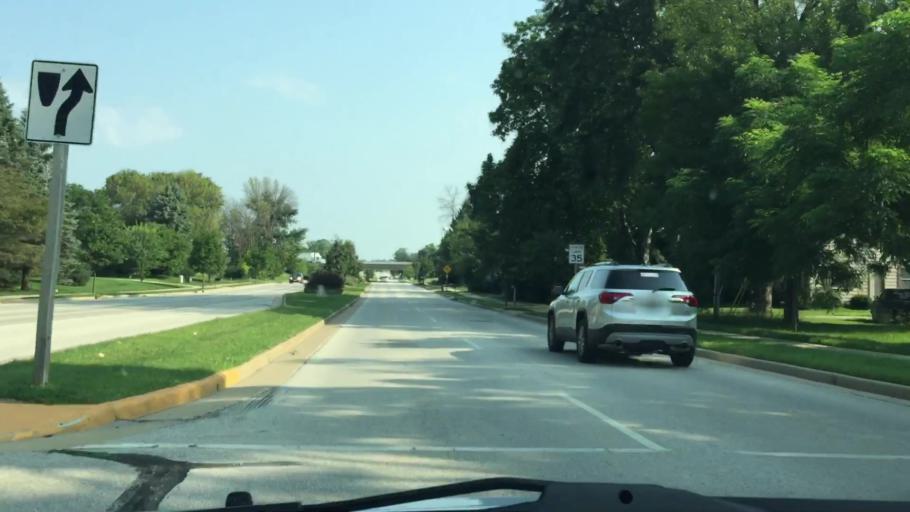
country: US
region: Wisconsin
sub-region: Waukesha County
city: Brookfield
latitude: 43.0251
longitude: -88.1269
